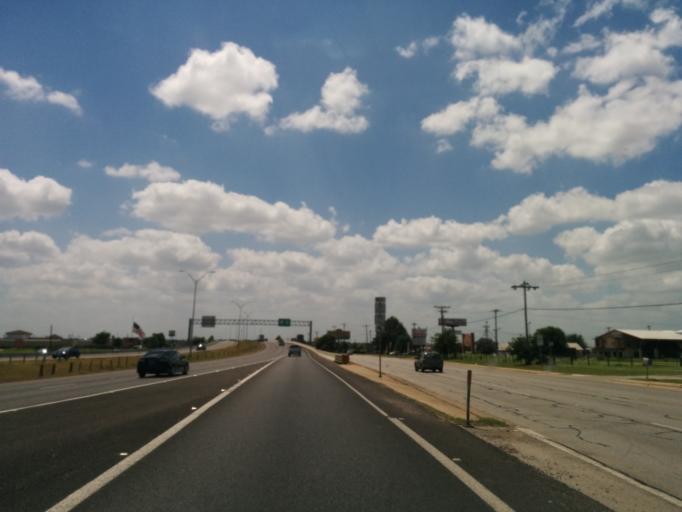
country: US
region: Texas
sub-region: Bastrop County
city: Bastrop
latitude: 30.1110
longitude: -97.3452
